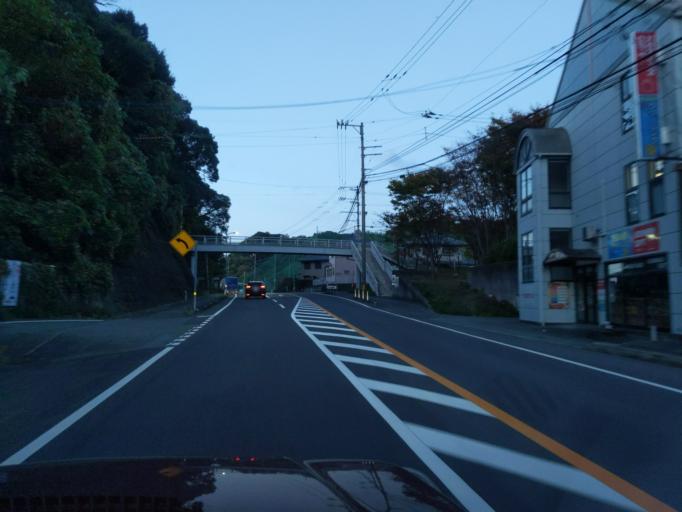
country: JP
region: Tokushima
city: Anan
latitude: 33.8707
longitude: 134.6344
